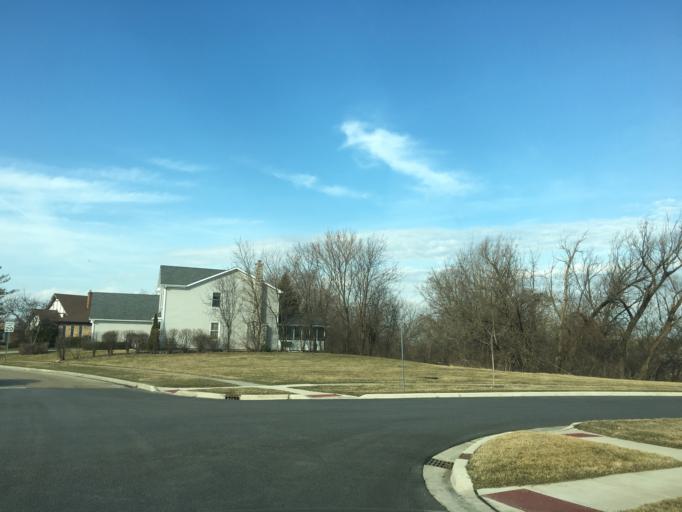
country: US
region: Illinois
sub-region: Cook County
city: Schaumburg
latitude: 42.0441
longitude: -88.1124
